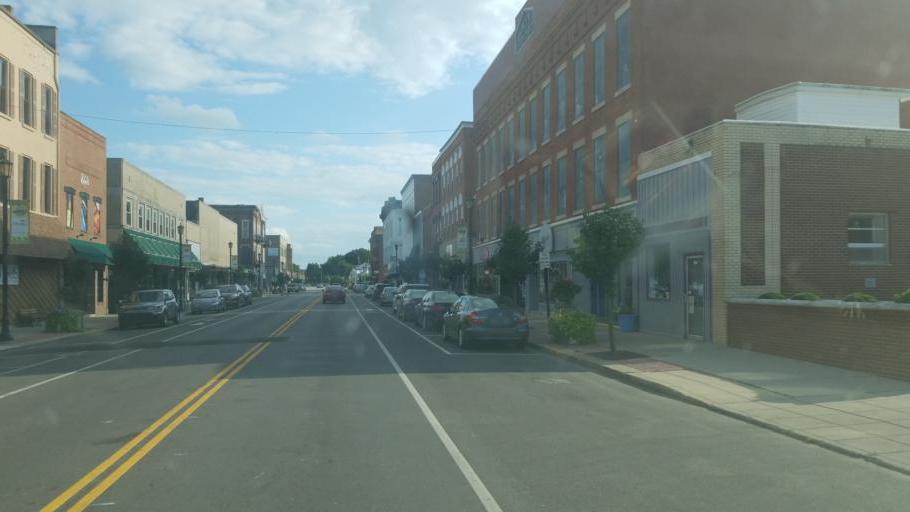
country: US
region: Ohio
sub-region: Sandusky County
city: Fremont
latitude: 41.3464
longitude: -83.1135
